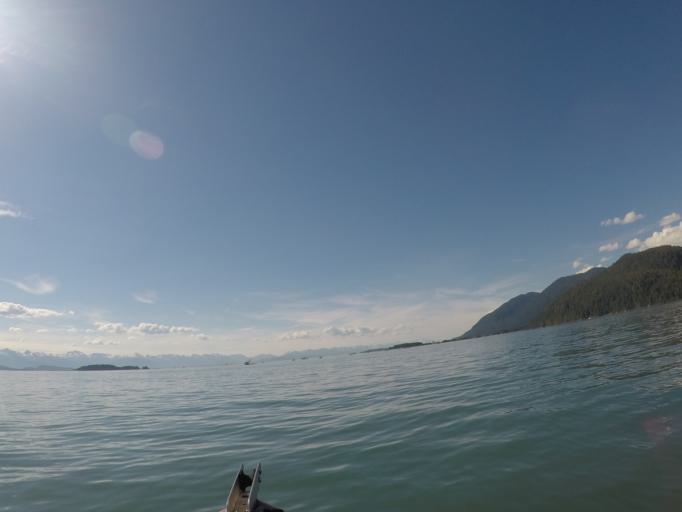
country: US
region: Alaska
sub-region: Juneau City and Borough
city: Juneau
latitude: 58.4931
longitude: -134.8128
